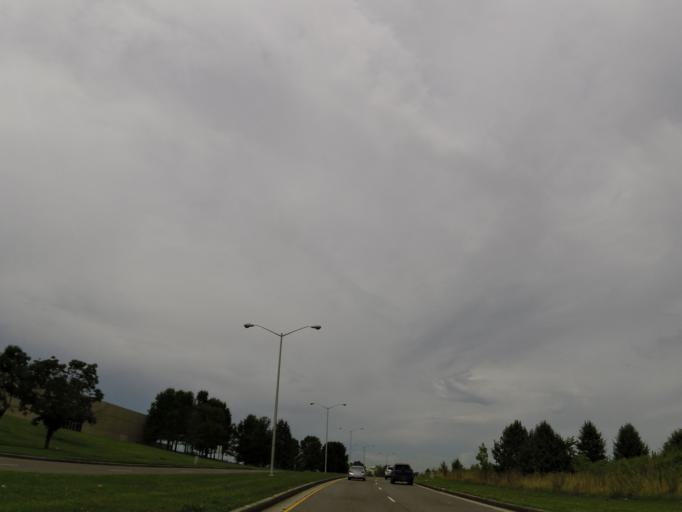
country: US
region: Tennessee
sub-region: Knox County
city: Farragut
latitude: 35.9047
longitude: -84.1361
